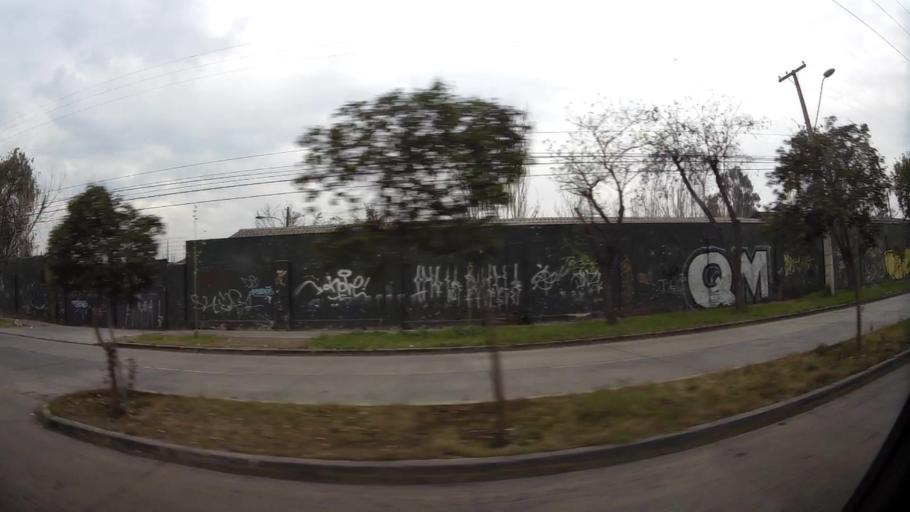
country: CL
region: Santiago Metropolitan
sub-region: Provincia de Santiago
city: Santiago
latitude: -33.4746
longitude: -70.6648
